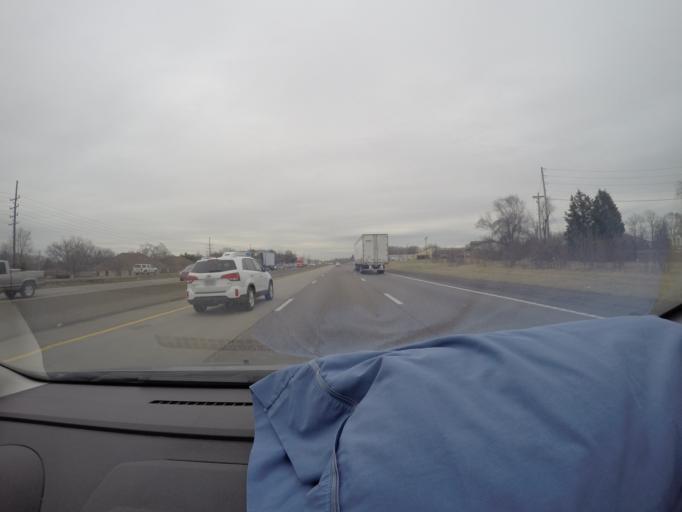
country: US
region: Missouri
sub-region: Saint Charles County
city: O'Fallon
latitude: 38.8025
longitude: -90.7135
